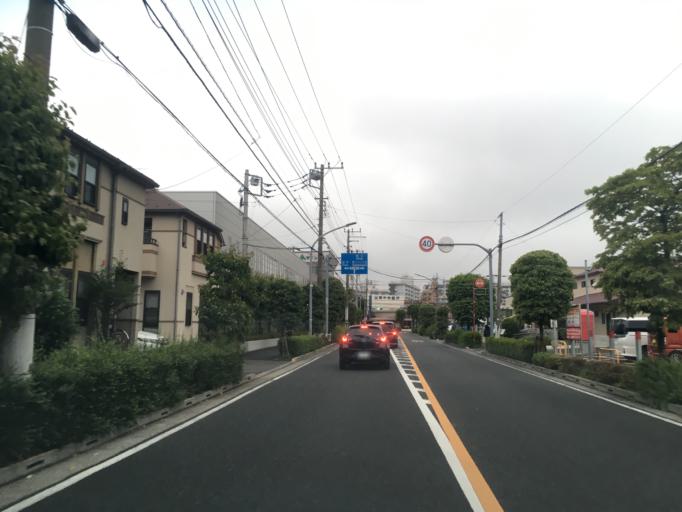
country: JP
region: Tokyo
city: Chofugaoka
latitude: 35.6440
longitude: 139.5600
